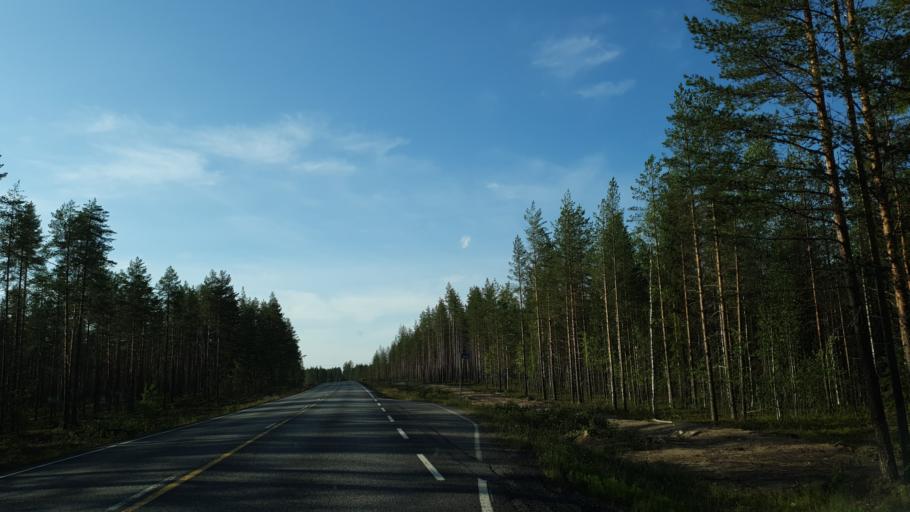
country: FI
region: Kainuu
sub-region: Kehys-Kainuu
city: Kuhmo
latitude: 64.0890
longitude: 29.4818
